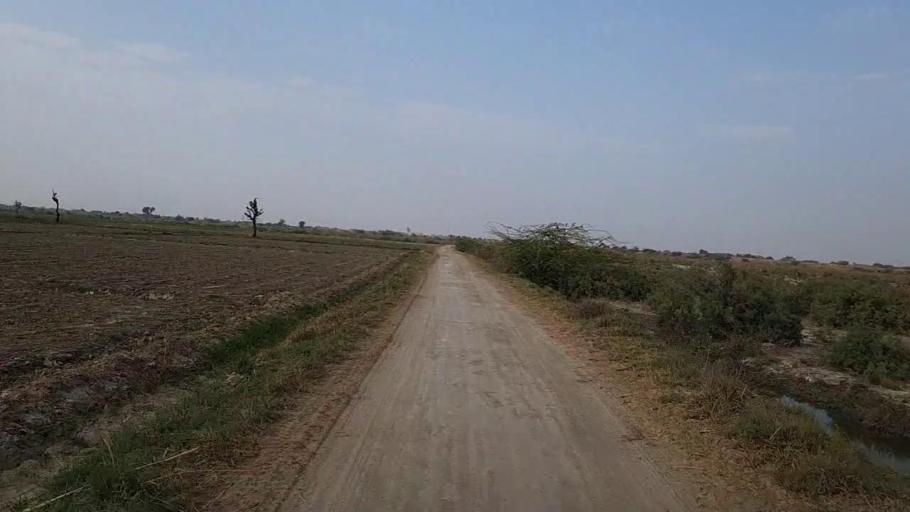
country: PK
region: Sindh
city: Pithoro
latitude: 25.4368
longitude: 69.2370
